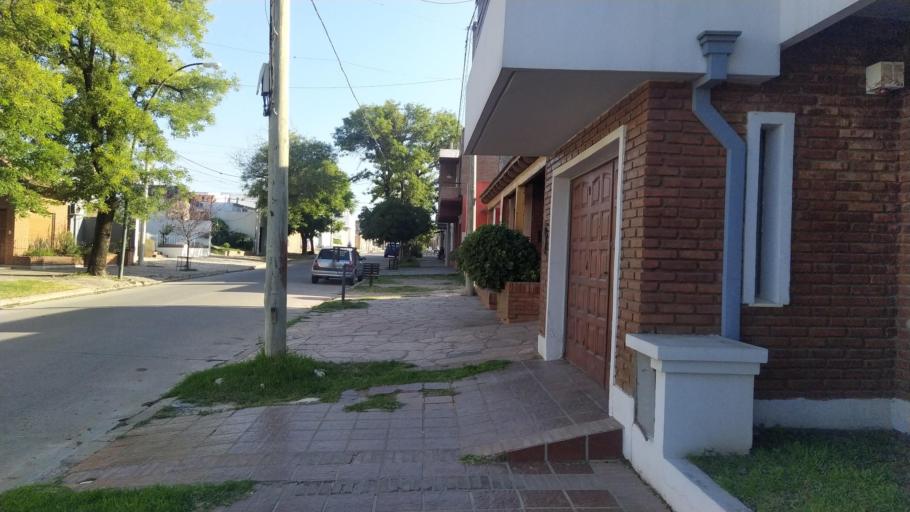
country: AR
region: Buenos Aires
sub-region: Partido de Salto
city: Salto
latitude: -34.2871
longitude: -60.2572
